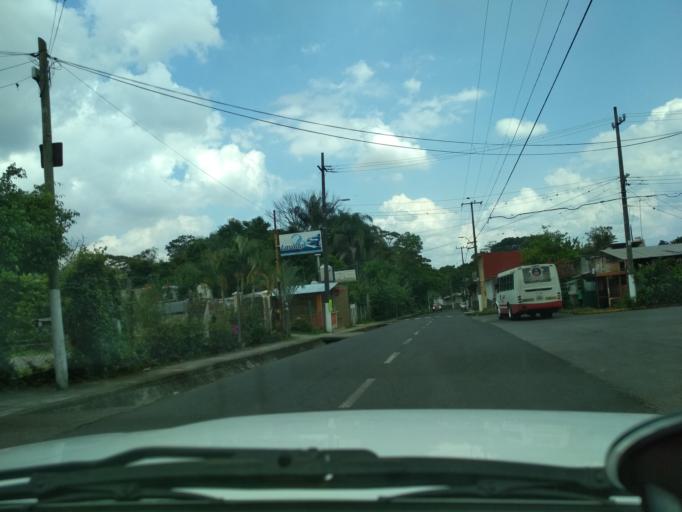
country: MX
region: Veracruz
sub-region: Cordoba
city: San Jose de Abajo [Unidad Habitacional]
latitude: 18.9208
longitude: -96.9624
